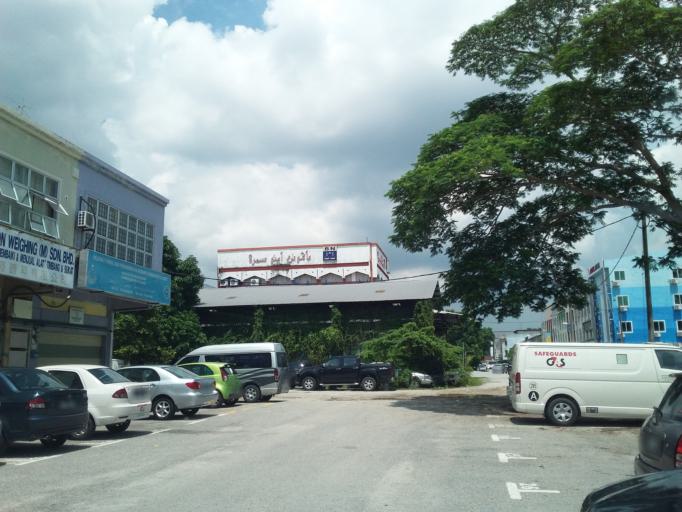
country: MY
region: Johor
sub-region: Daerah Batu Pahat
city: Batu Pahat
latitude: 1.8577
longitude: 102.9258
